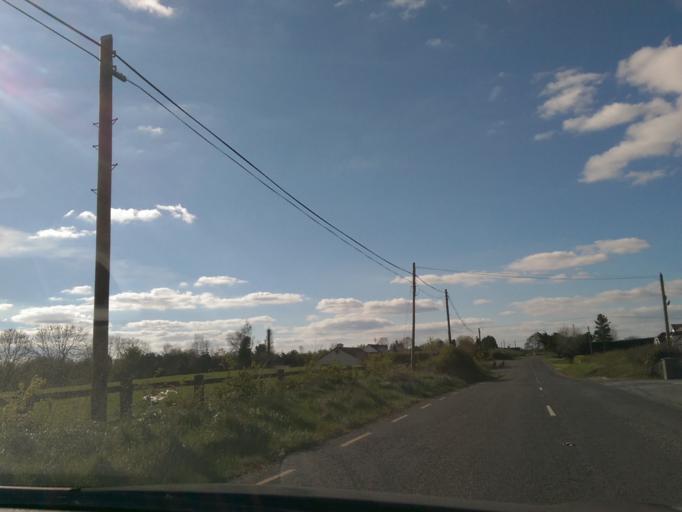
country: IE
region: Leinster
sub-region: Uibh Fhaili
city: Birr
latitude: 53.0938
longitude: -7.9642
